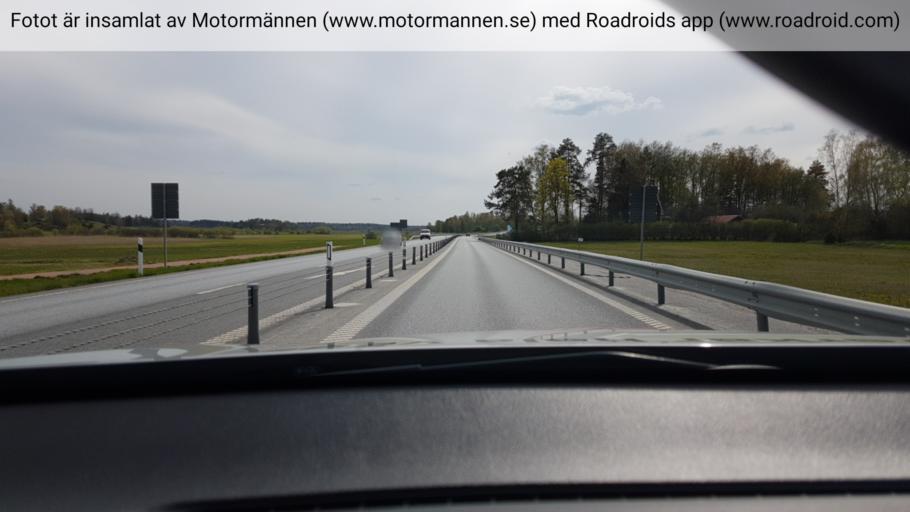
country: SE
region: Uppsala
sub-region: Osthammars Kommun
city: Gimo
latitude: 60.0455
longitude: 18.0455
